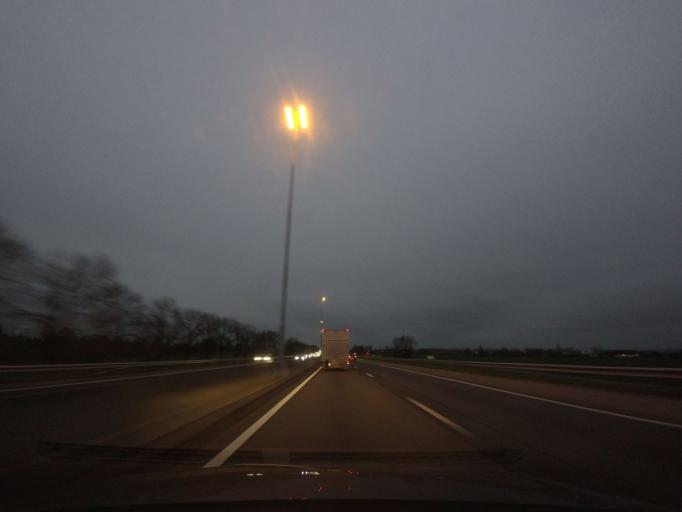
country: NL
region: Utrecht
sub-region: Gemeente Lopik
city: Lopik
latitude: 51.9305
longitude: 4.9953
